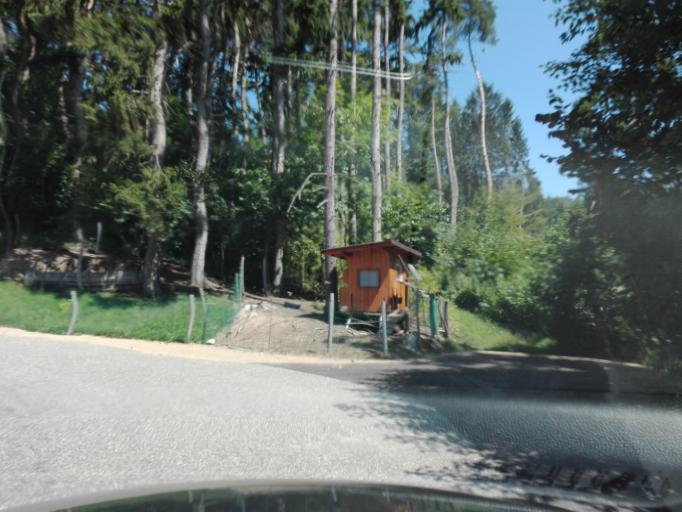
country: AT
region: Upper Austria
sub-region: Politischer Bezirk Urfahr-Umgebung
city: Gallneukirchen
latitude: 48.3107
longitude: 14.4078
